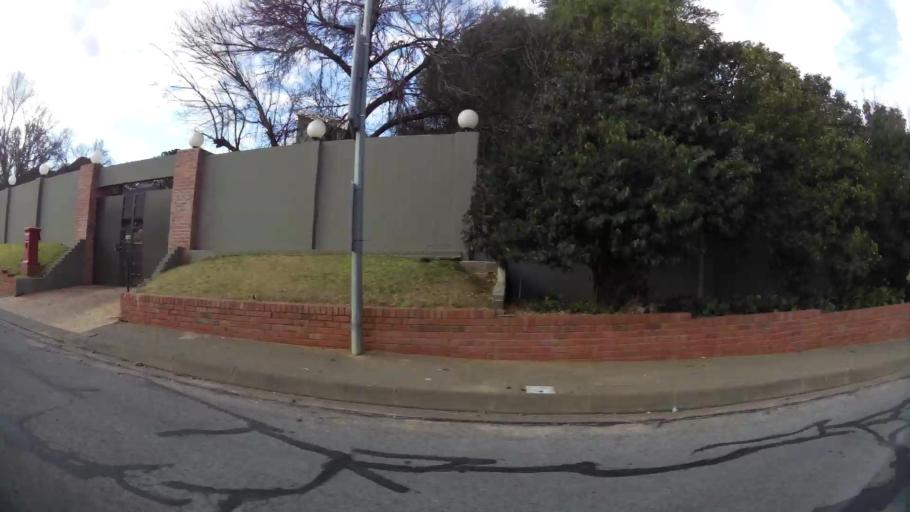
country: ZA
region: Orange Free State
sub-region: Mangaung Metropolitan Municipality
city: Bloemfontein
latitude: -29.0789
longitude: 26.2062
